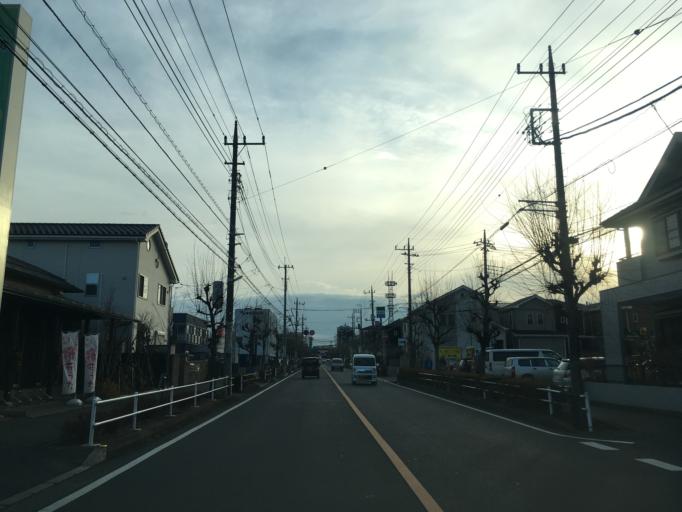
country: JP
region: Saitama
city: Tokorozawa
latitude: 35.8000
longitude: 139.4561
